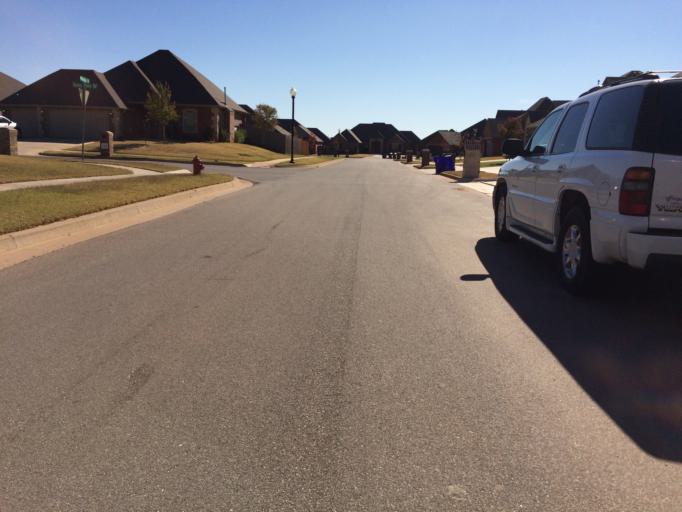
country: US
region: Oklahoma
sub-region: Cleveland County
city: Noble
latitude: 35.1702
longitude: -97.4231
